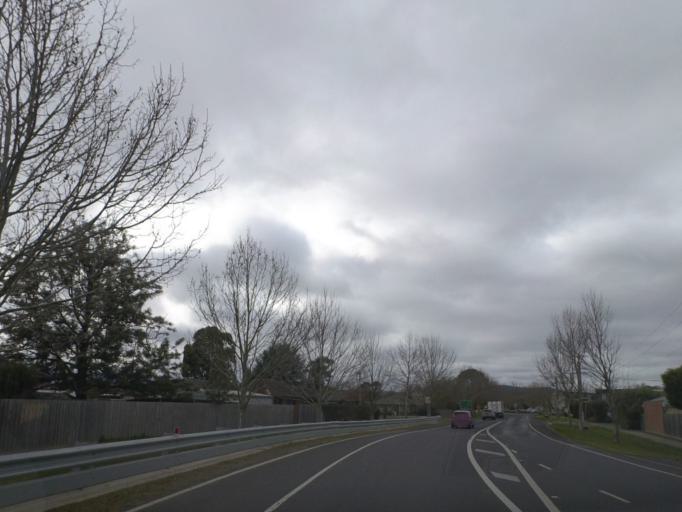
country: AU
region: Victoria
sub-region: Whittlesea
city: Whittlesea
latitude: -37.5107
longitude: 145.1161
